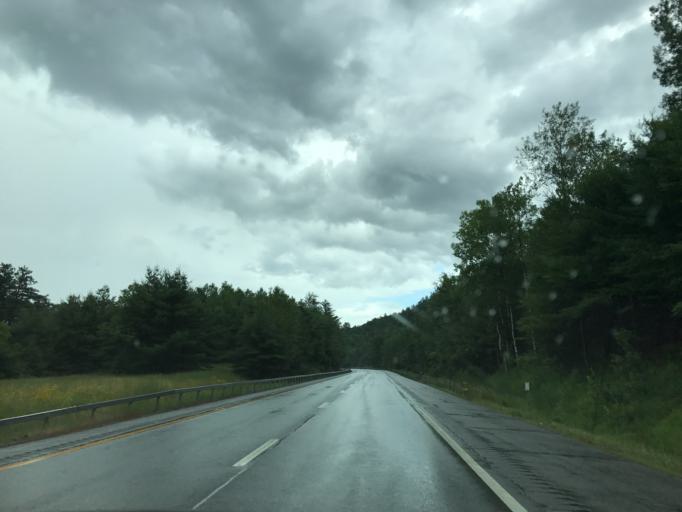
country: US
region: New York
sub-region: Warren County
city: Warrensburg
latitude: 43.5025
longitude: -73.7451
